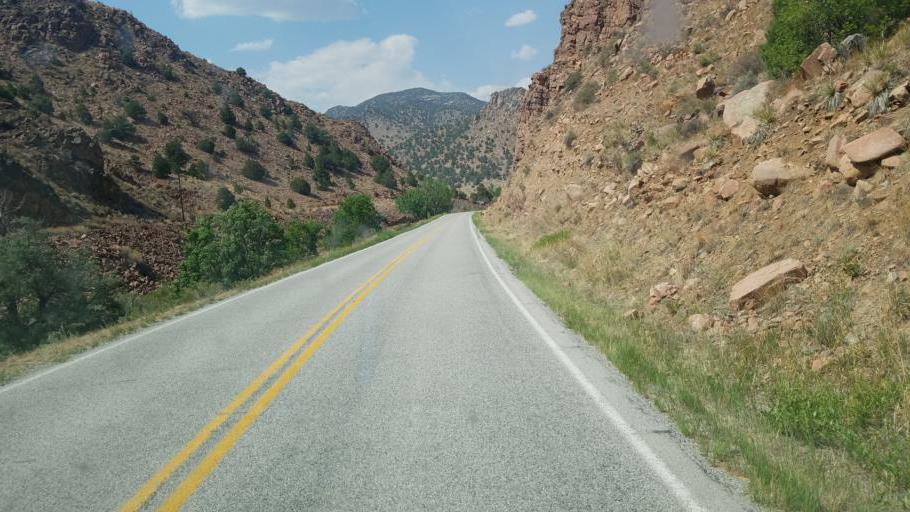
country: US
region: Colorado
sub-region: Custer County
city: Westcliffe
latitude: 38.4051
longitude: -105.5847
